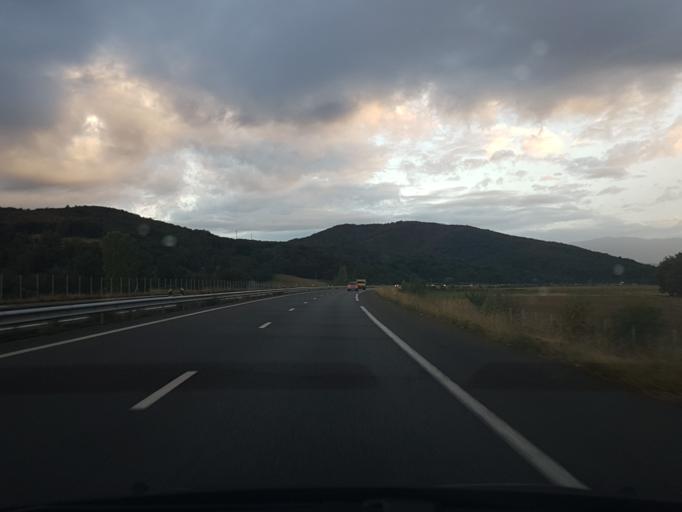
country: FR
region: Midi-Pyrenees
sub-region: Departement de l'Ariege
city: Varilhes
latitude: 43.0506
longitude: 1.6490
